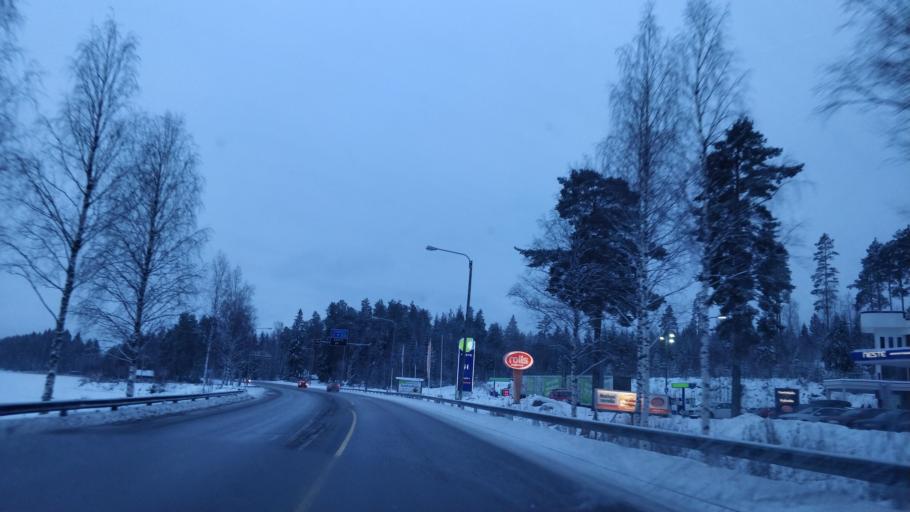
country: FI
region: Central Finland
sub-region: AEaenekoski
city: AEaenekoski
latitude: 62.8200
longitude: 25.8030
